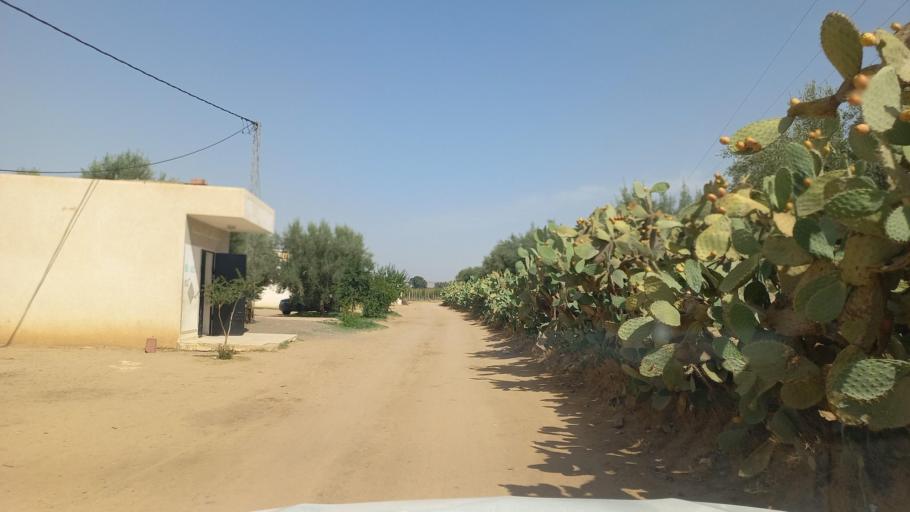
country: TN
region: Al Qasrayn
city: Kasserine
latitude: 35.2547
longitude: 9.0447
